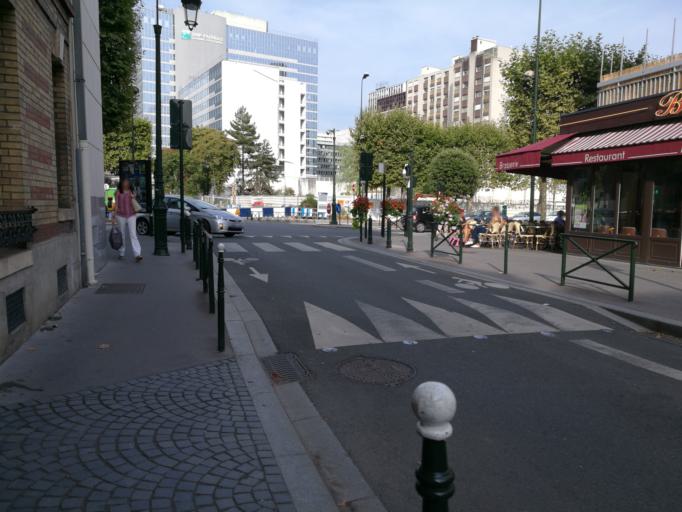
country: FR
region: Ile-de-France
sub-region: Departement des Hauts-de-Seine
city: Puteaux
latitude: 48.8851
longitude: 2.2467
